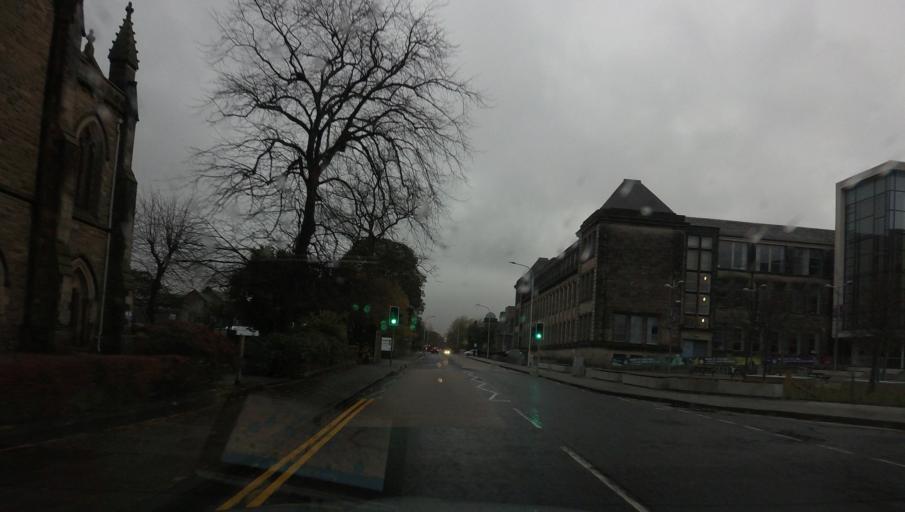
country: GB
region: Scotland
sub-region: Fife
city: Kirkcaldy
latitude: 56.1128
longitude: -3.1609
